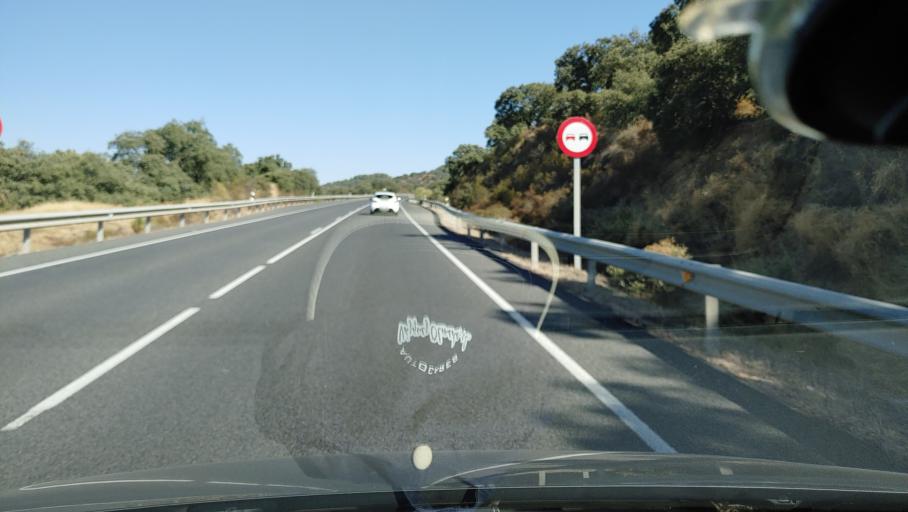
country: ES
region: Andalusia
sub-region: Province of Cordoba
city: Obejo
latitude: 38.0181
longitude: -4.8081
